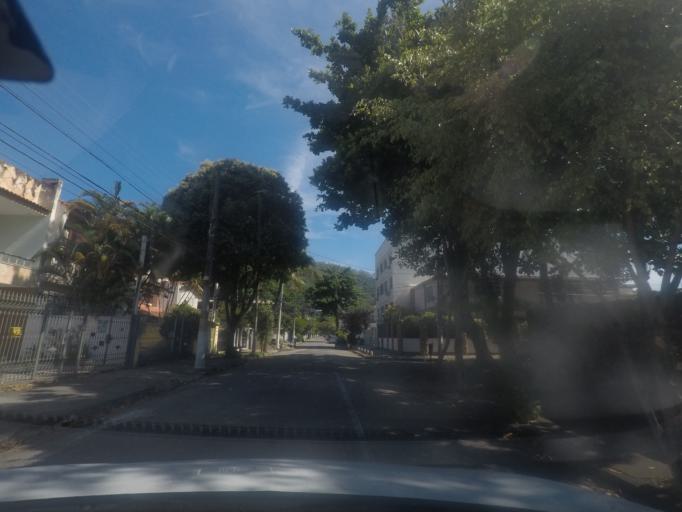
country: BR
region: Rio de Janeiro
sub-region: Niteroi
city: Niteroi
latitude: -22.9167
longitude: -43.0904
